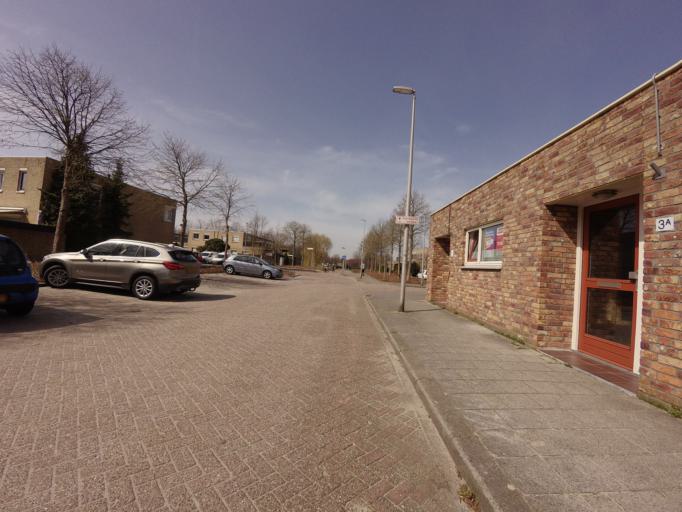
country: NL
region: South Holland
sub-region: Gemeente Rijnwoude
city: Benthuizen
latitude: 52.0737
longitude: 4.5222
